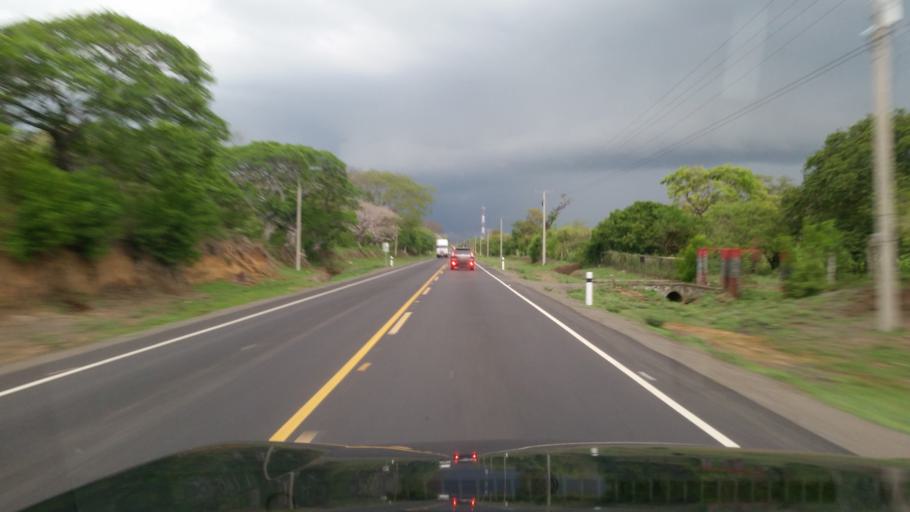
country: NI
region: Leon
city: Nagarote
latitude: 12.2711
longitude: -86.5369
